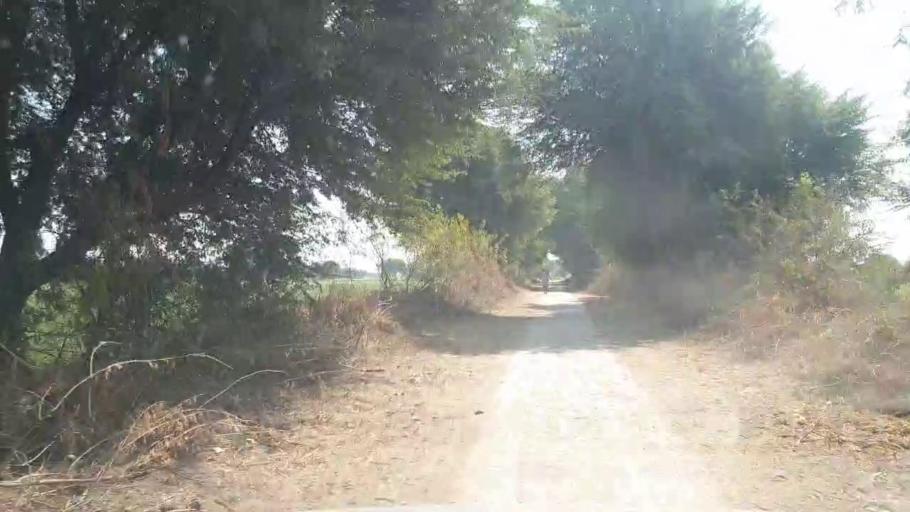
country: PK
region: Sindh
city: Chambar
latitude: 25.2737
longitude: 68.8137
